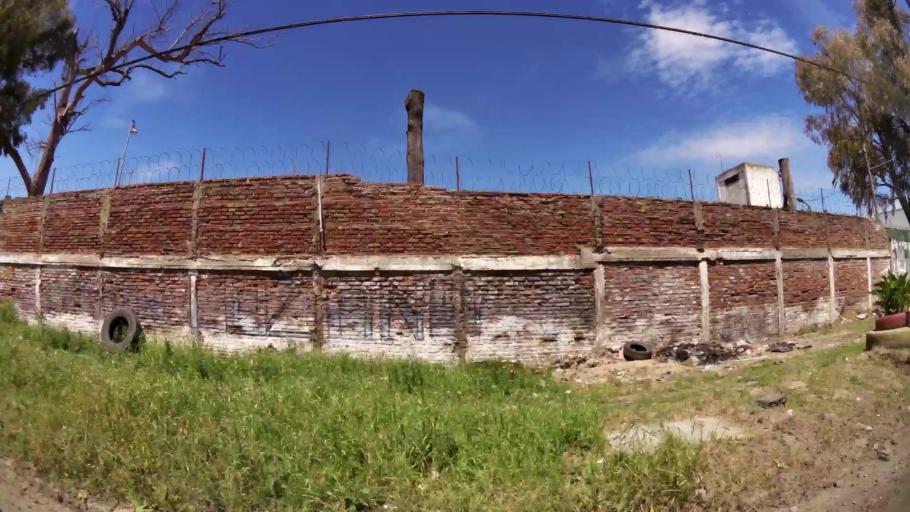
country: AR
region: Buenos Aires
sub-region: Partido de Quilmes
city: Quilmes
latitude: -34.7310
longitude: -58.3221
